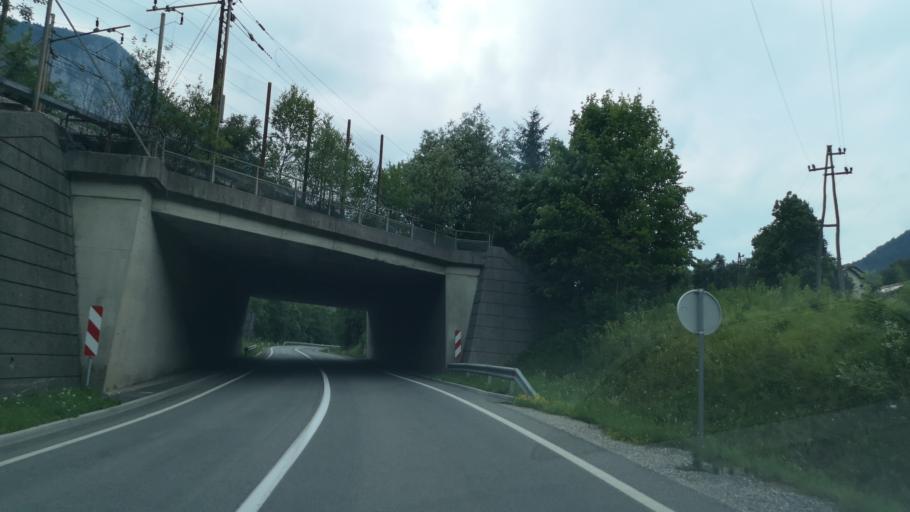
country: SI
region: Jesenice
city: Hrusica
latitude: 46.4461
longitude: 14.0240
